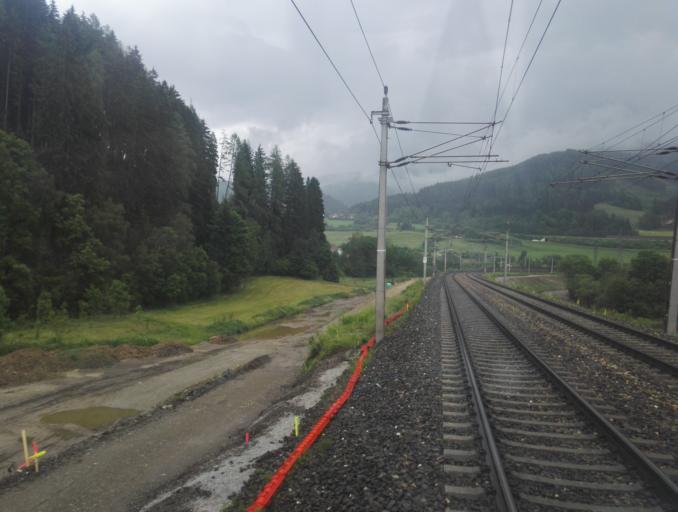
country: AT
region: Styria
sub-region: Politischer Bezirk Bruck-Muerzzuschlag
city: Kindberg
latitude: 47.5199
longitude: 15.4691
